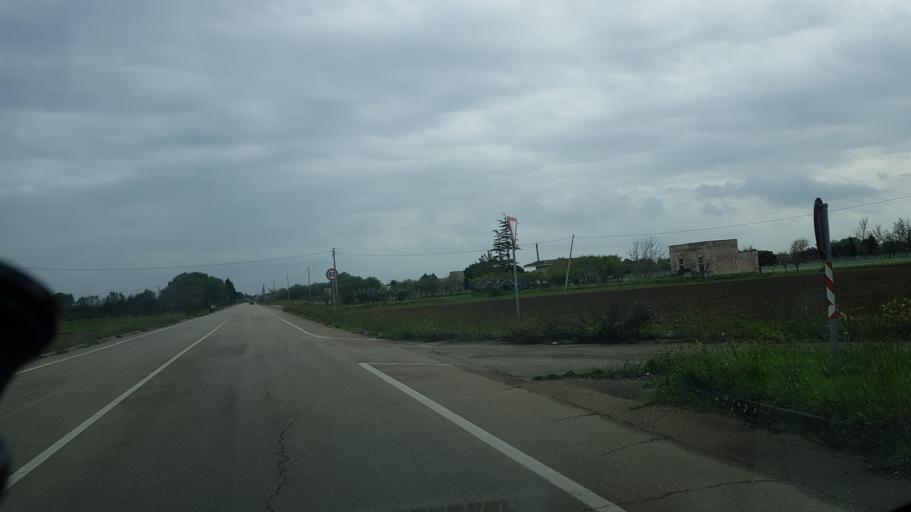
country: IT
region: Apulia
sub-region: Provincia di Lecce
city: Campi Salentina
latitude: 40.3839
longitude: 18.0227
